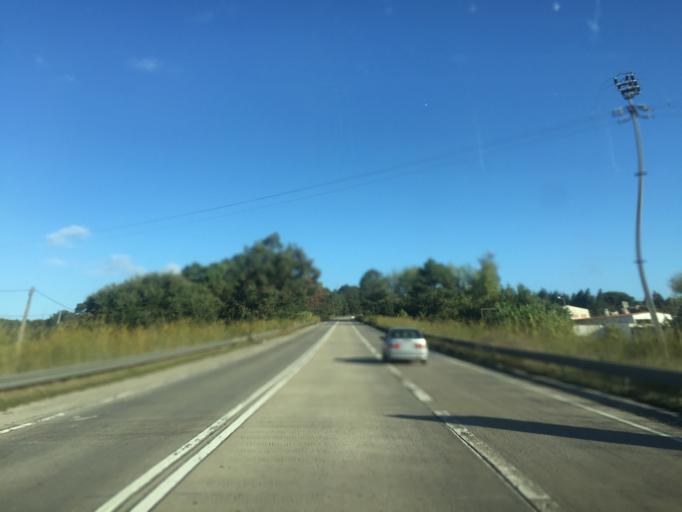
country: PT
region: Santarem
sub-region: Rio Maior
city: Rio Maior
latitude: 39.2967
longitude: -8.9480
